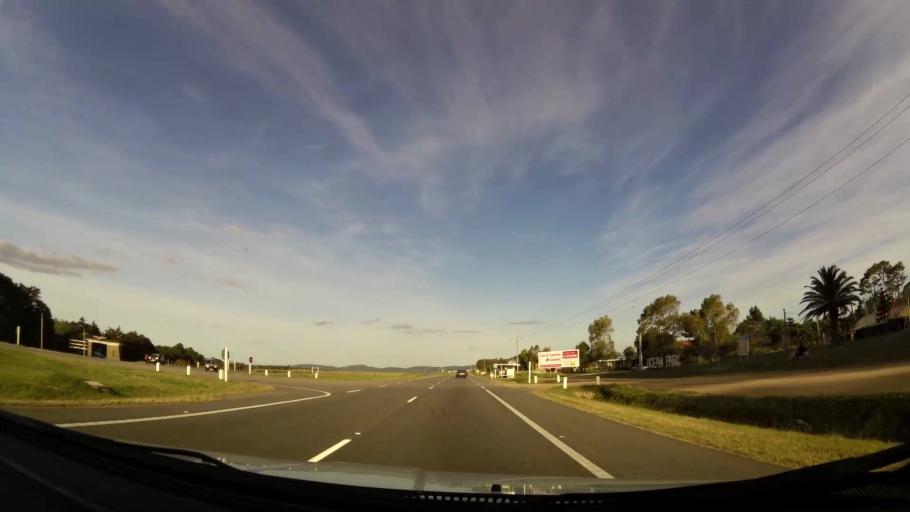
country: UY
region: Maldonado
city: Pan de Azucar
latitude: -34.8636
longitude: -55.1246
